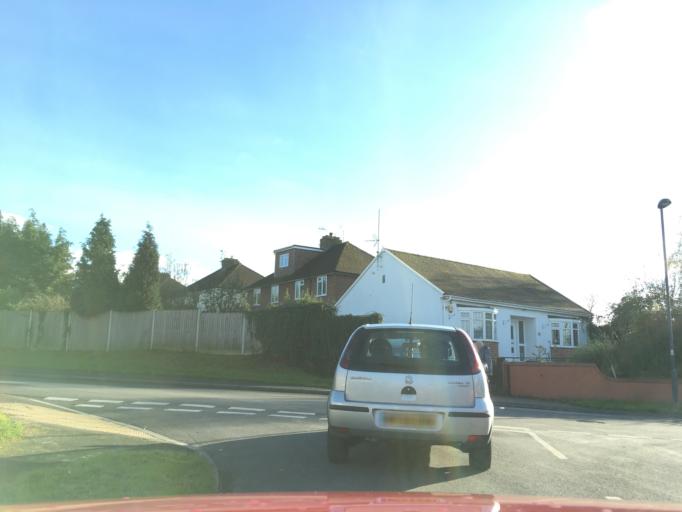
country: GB
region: England
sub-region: South Gloucestershire
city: Thornbury
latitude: 51.6127
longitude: -2.5163
